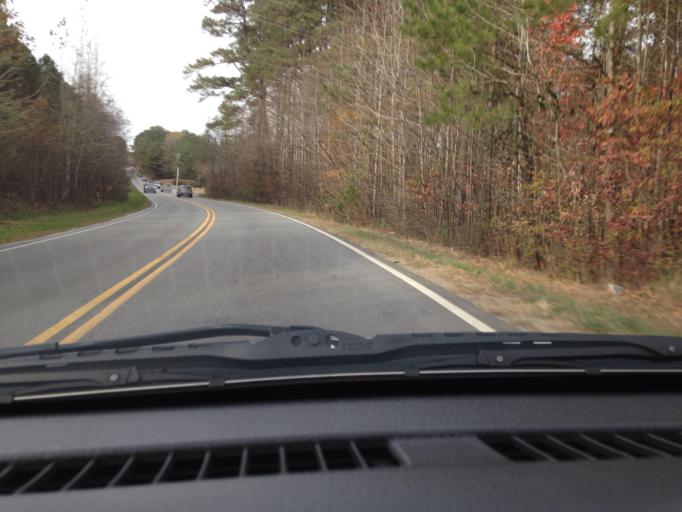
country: US
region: Georgia
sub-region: Fulton County
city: Johns Creek
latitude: 34.0728
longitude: -84.1797
